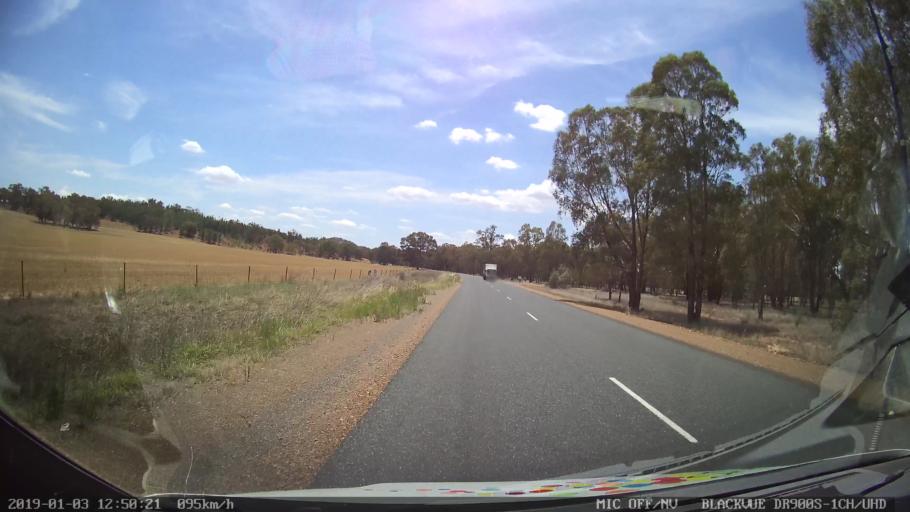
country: AU
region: New South Wales
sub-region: Weddin
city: Grenfell
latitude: -33.6925
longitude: 148.2694
